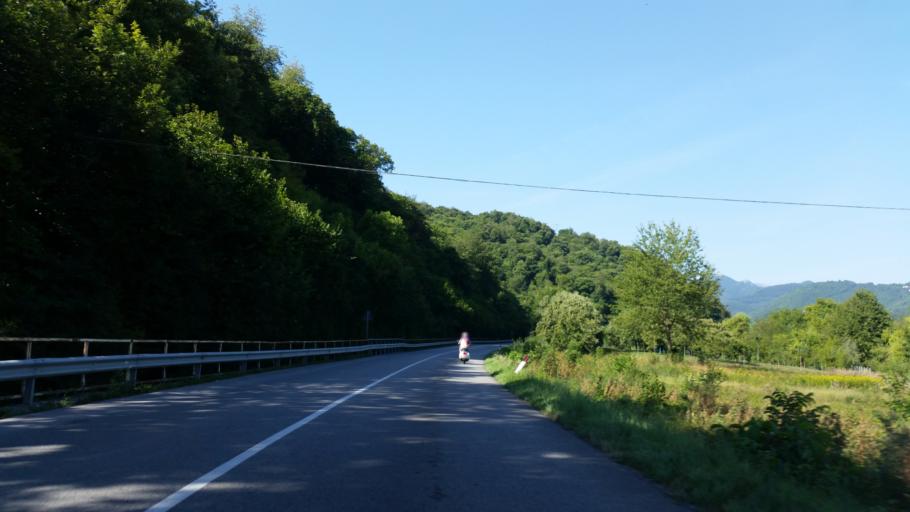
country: IT
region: Piedmont
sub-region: Provincia di Cuneo
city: Borgo San Dalmazzo
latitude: 44.3292
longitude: 7.5135
